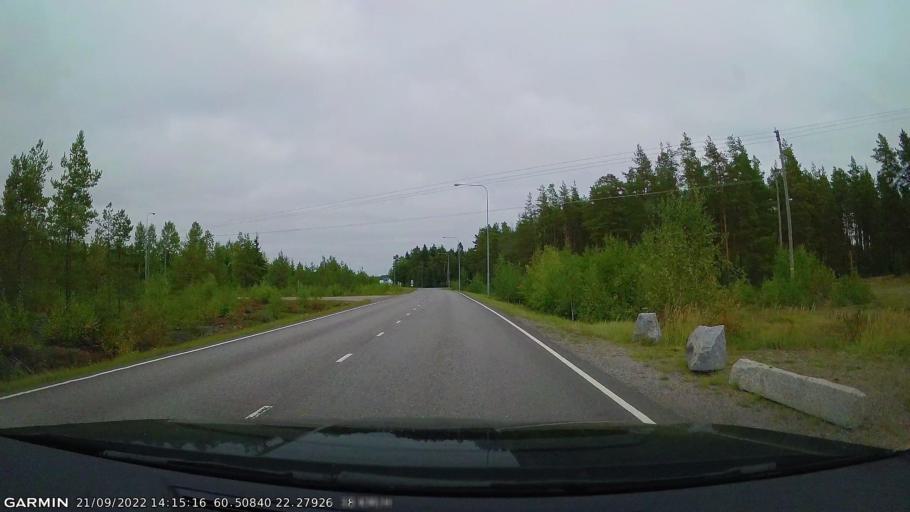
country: FI
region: Varsinais-Suomi
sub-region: Turku
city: Turku
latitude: 60.5086
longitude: 22.2793
